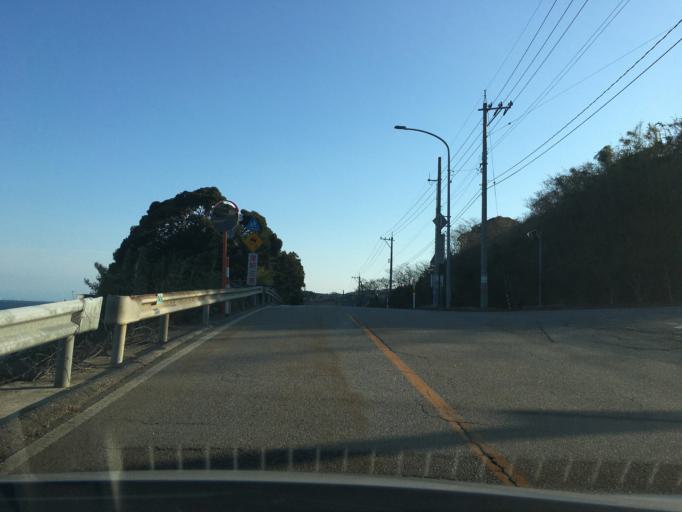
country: JP
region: Ishikawa
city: Nanao
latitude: 36.9923
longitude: 137.0528
